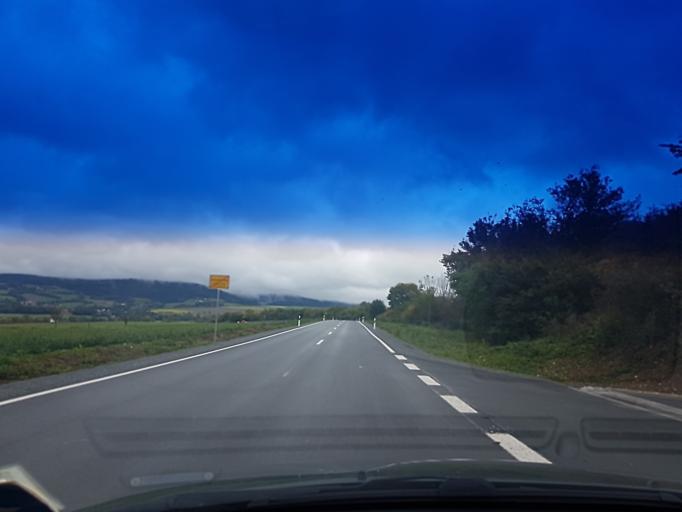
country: DE
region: Bavaria
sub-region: Upper Franconia
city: Bindlach
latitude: 49.9904
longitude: 11.6392
